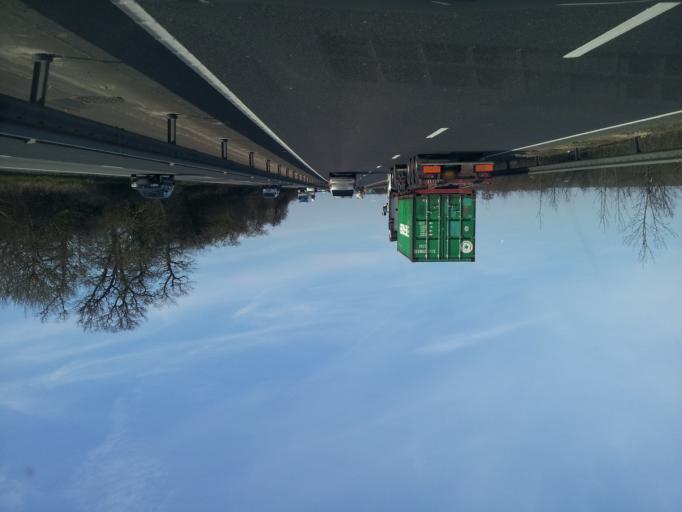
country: GB
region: England
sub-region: Bedford
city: Pertenhall
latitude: 52.3534
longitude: -0.3833
